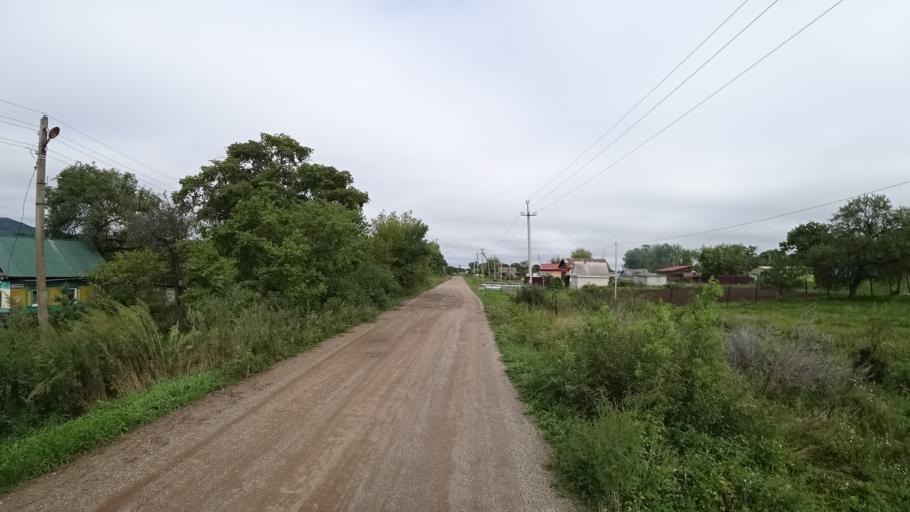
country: RU
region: Primorskiy
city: Lyalichi
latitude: 44.0783
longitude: 132.4764
